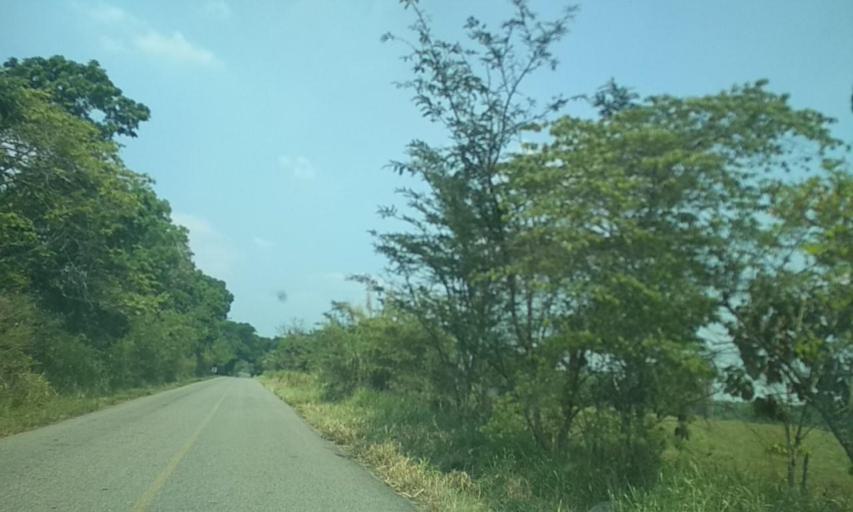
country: MX
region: Tabasco
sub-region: Cardenas
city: Poblado C-33 20 de Noviembre
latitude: 17.8417
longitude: -93.5547
